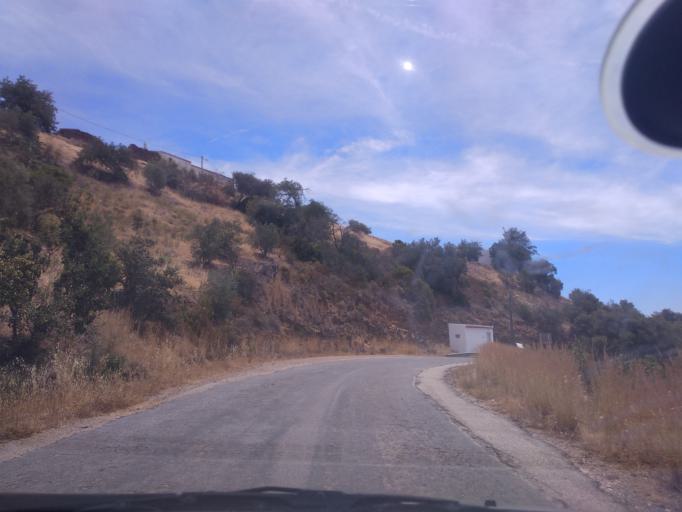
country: PT
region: Faro
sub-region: Olhao
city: Moncarapacho
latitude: 37.1551
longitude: -7.7963
